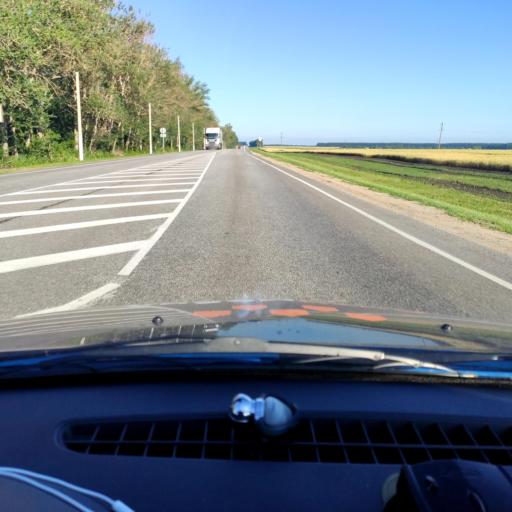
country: RU
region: Orjol
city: Pokrovskoye
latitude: 52.6290
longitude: 36.7073
